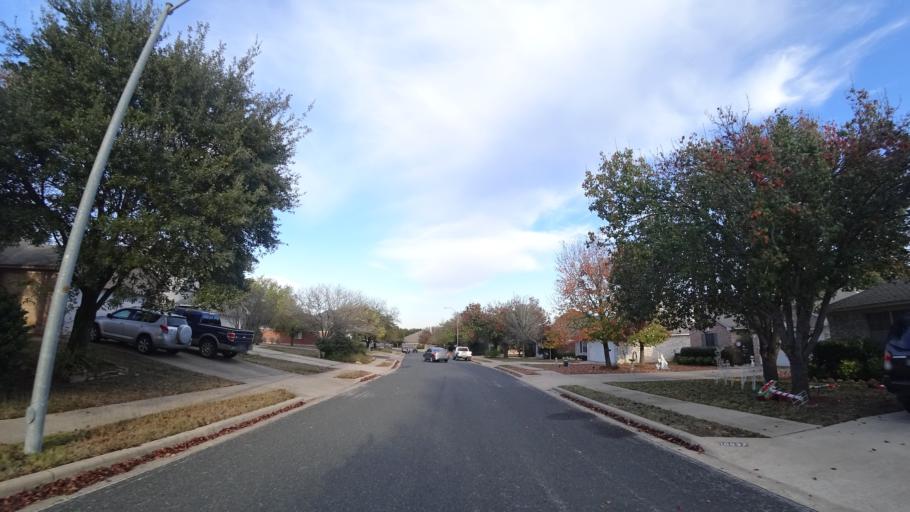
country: US
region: Texas
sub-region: Williamson County
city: Brushy Creek
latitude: 30.5009
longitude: -97.7317
